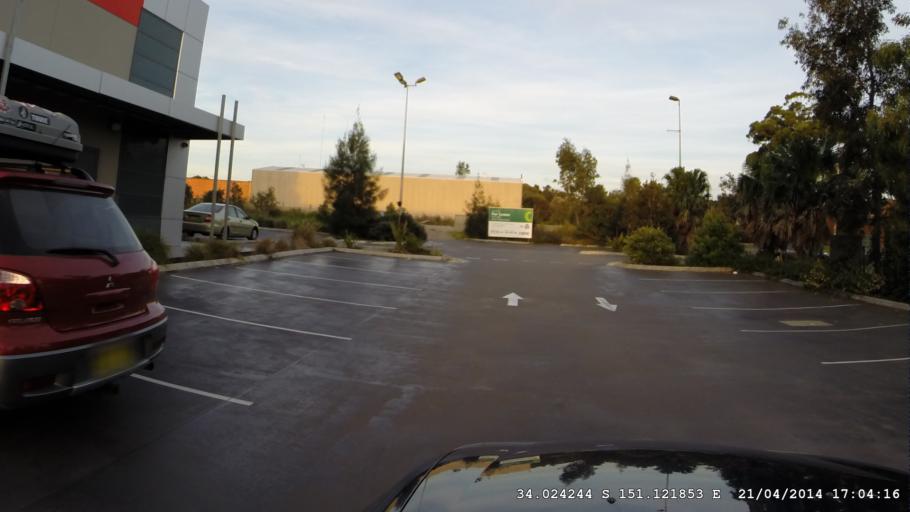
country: AU
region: New South Wales
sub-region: Sutherland Shire
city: Caringbah
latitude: -34.0242
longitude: 151.1219
